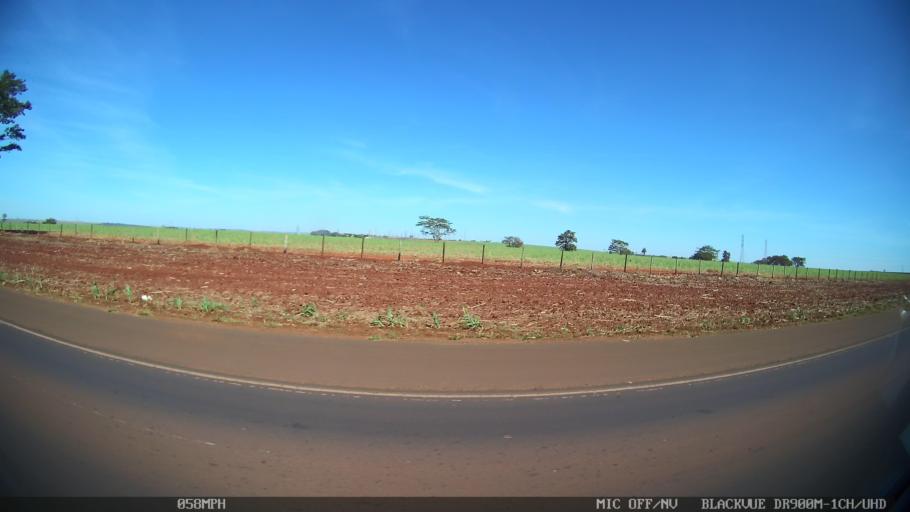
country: BR
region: Sao Paulo
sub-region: Sao Joaquim Da Barra
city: Sao Joaquim da Barra
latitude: -20.5222
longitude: -47.8468
